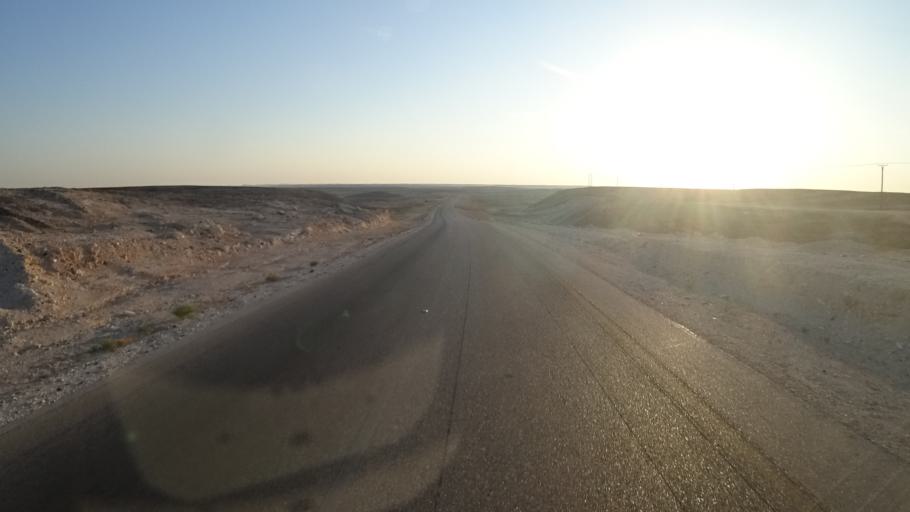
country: OM
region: Zufar
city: Salalah
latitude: 17.5336
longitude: 53.4048
